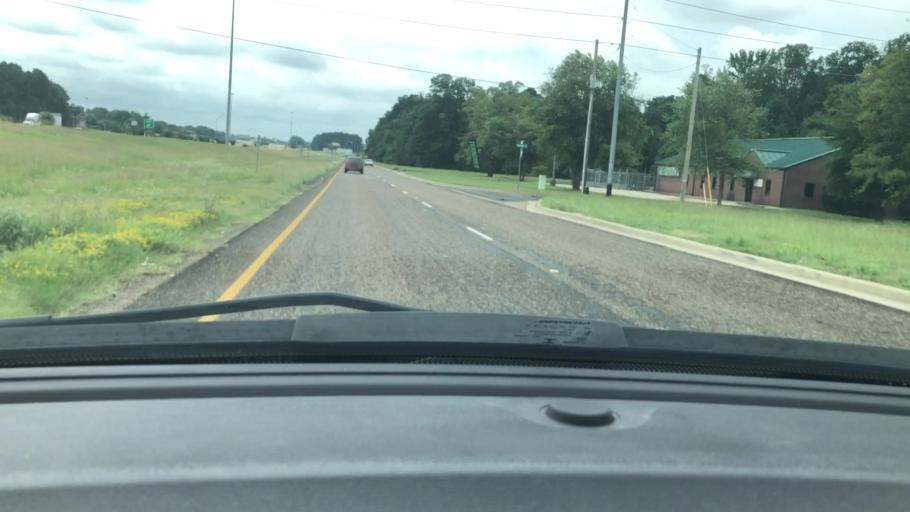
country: US
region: Texas
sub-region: Bowie County
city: Wake Village
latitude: 33.4403
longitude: -94.0974
